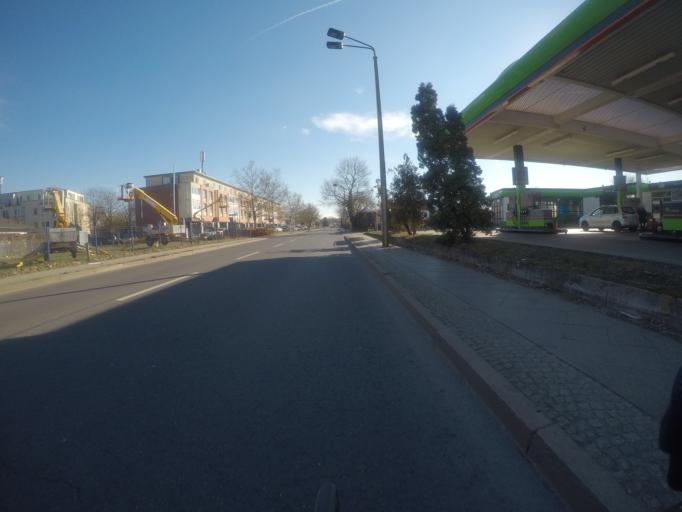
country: DE
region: Berlin
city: Kopenick Bezirk
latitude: 52.4720
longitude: 13.5716
